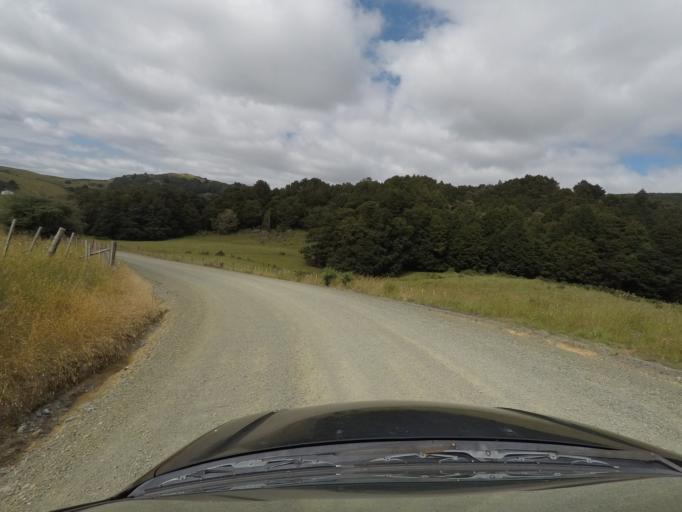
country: NZ
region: Northland
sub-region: Whangarei
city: Ruakaka
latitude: -35.9315
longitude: 174.3455
